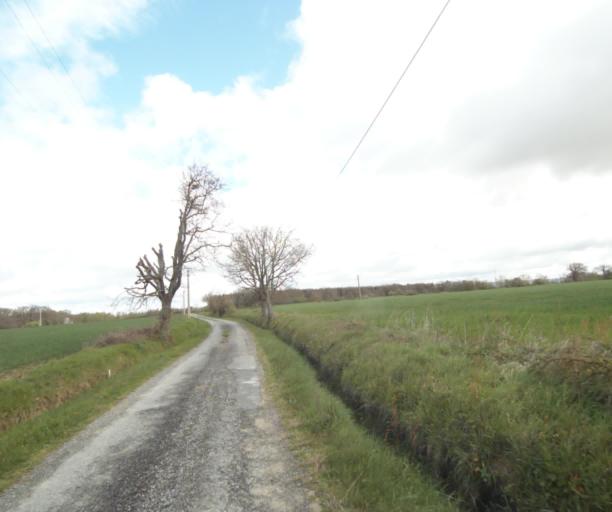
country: FR
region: Midi-Pyrenees
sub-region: Departement de l'Ariege
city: Saverdun
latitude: 43.2368
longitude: 1.5485
